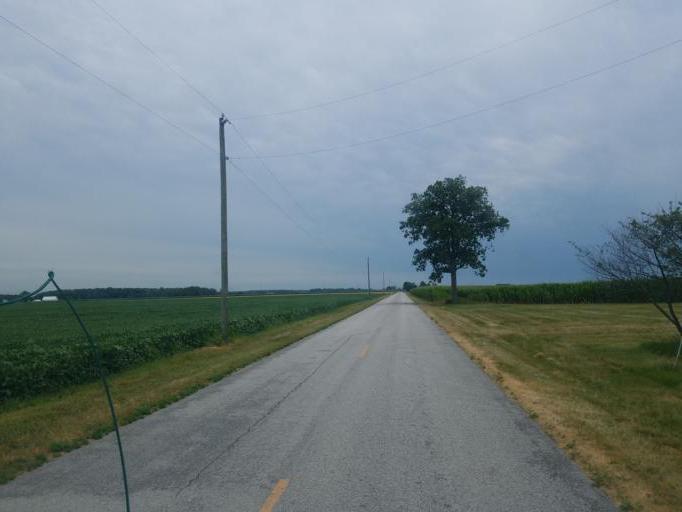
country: US
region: Ohio
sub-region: Defiance County
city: Hicksville
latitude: 41.2372
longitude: -84.7649
